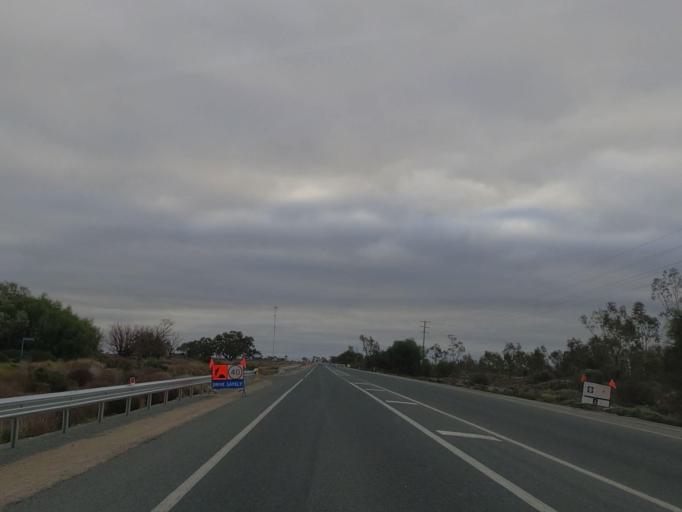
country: AU
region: Victoria
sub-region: Swan Hill
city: Swan Hill
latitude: -35.5345
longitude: 143.7439
